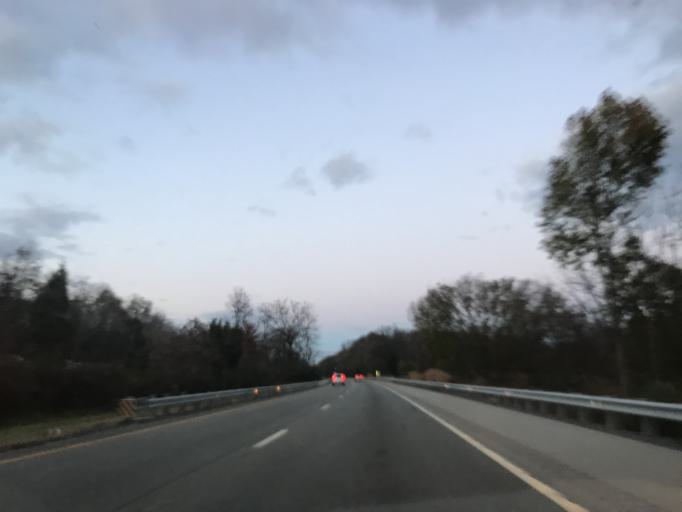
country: US
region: Delaware
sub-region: New Castle County
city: Bellefonte
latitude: 39.7912
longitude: -75.4911
